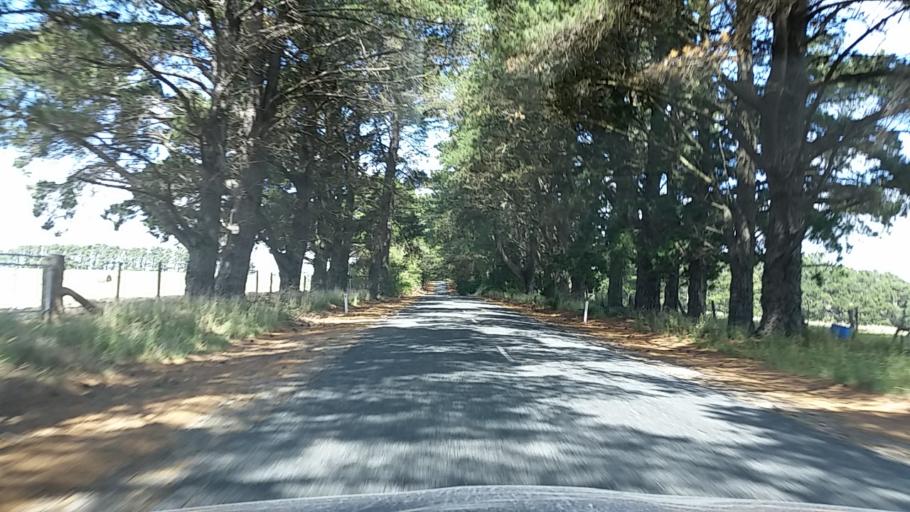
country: AU
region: South Australia
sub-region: Alexandrina
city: Mount Compass
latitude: -35.4407
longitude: 138.6200
